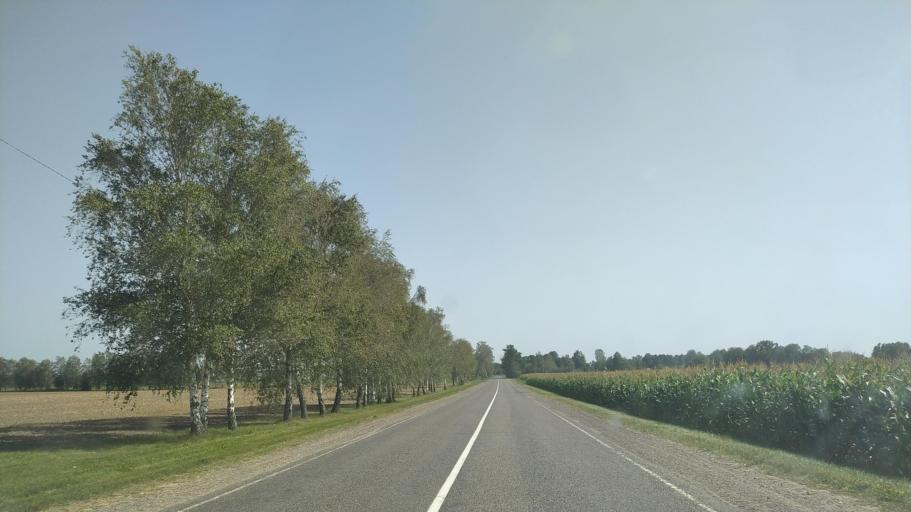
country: BY
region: Brest
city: Byaroza
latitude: 52.3951
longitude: 25.0085
